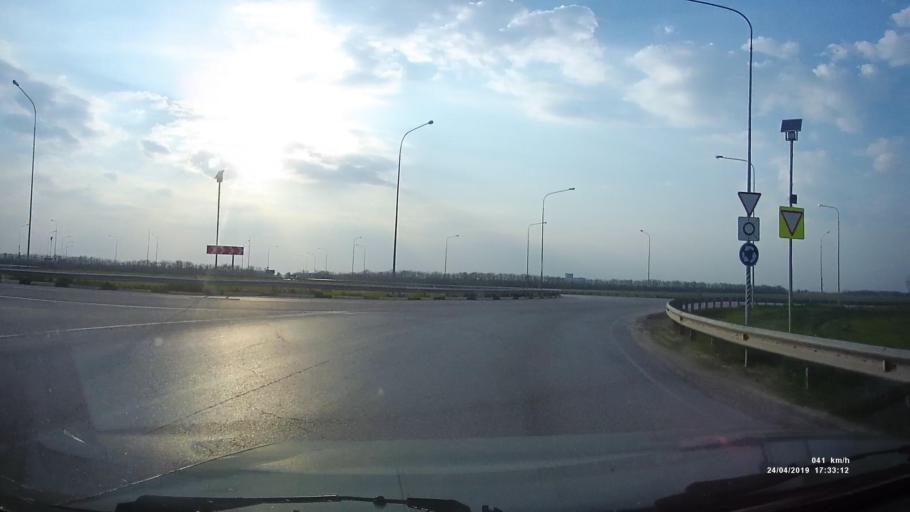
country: RU
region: Rostov
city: Tselina
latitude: 46.5264
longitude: 41.0823
